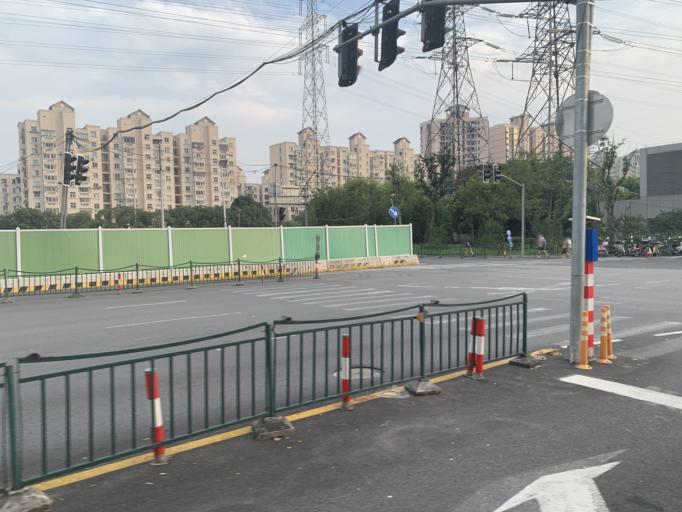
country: CN
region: Shanghai Shi
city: Huamu
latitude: 31.2432
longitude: 121.5738
